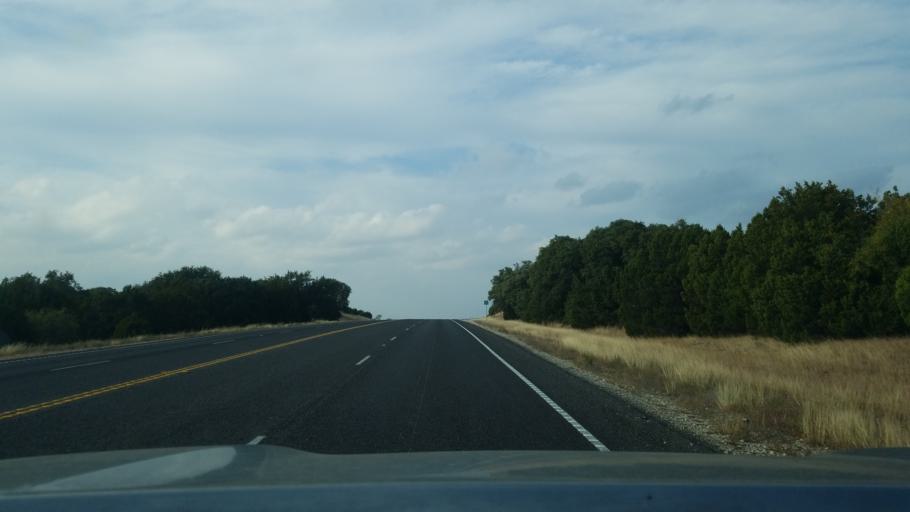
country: US
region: Texas
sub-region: Mills County
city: Goldthwaite
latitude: 31.3362
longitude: -98.4969
